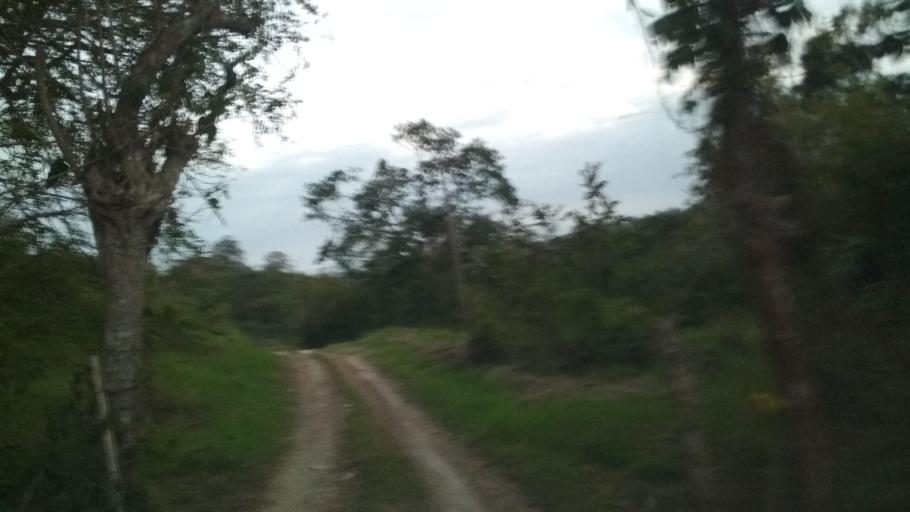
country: MX
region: Veracruz
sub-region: Poza Rica de Hidalgo
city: Arroyo del Maiz Uno
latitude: 20.4862
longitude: -97.3902
